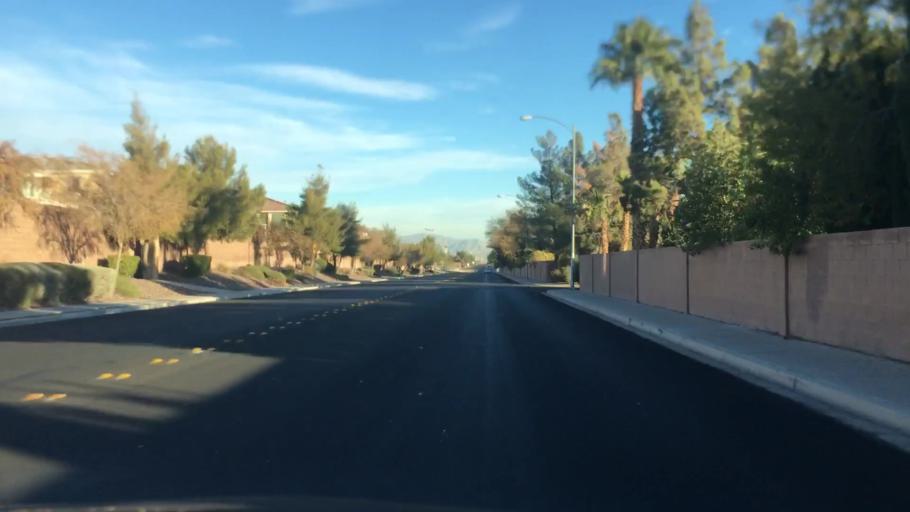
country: US
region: Nevada
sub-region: Clark County
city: Paradise
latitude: 36.0465
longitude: -115.1499
